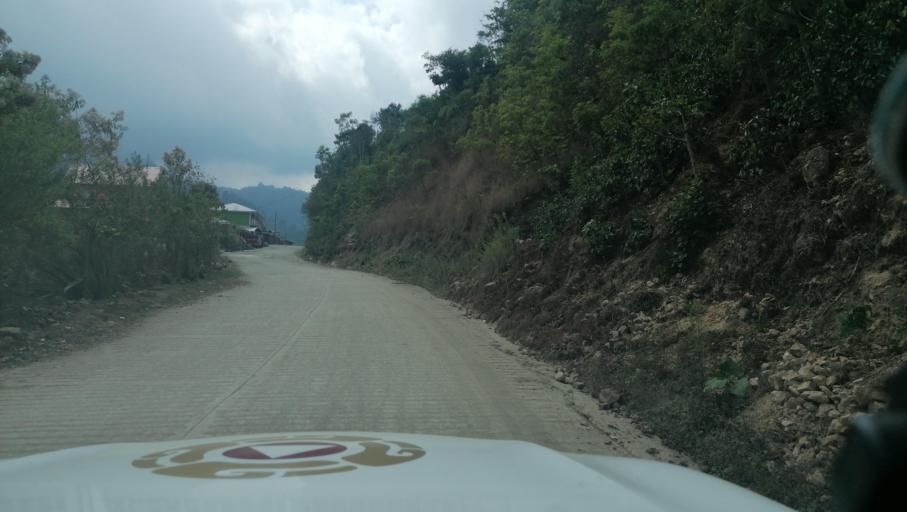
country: GT
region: San Marcos
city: Tacana
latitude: 15.2118
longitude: -92.1947
